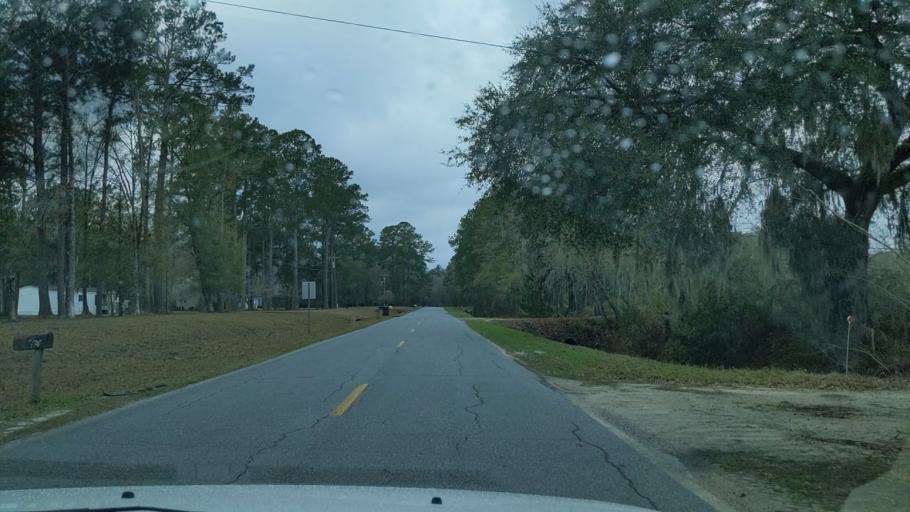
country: US
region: Georgia
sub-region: Chatham County
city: Georgetown
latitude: 32.0351
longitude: -81.3053
